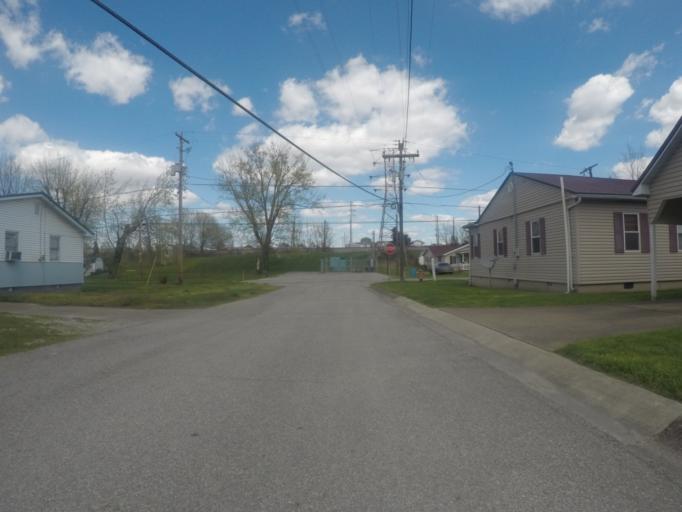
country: US
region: West Virginia
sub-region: Wayne County
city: Kenova
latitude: 38.3994
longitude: -82.5860
